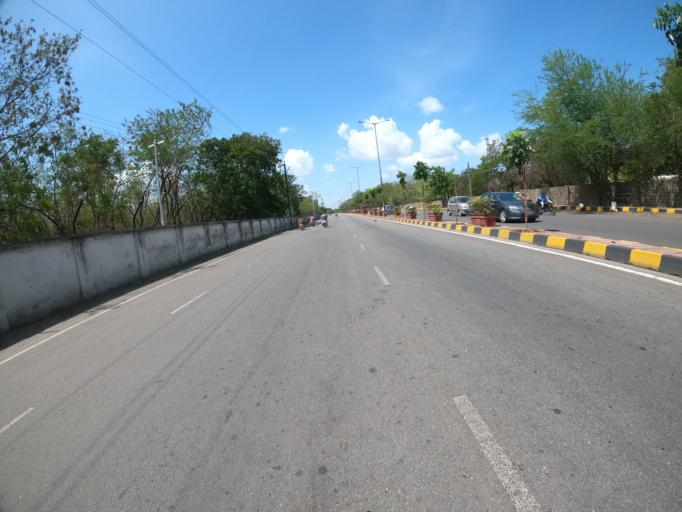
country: IN
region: Telangana
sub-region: Hyderabad
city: Hyderabad
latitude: 17.3872
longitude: 78.4228
